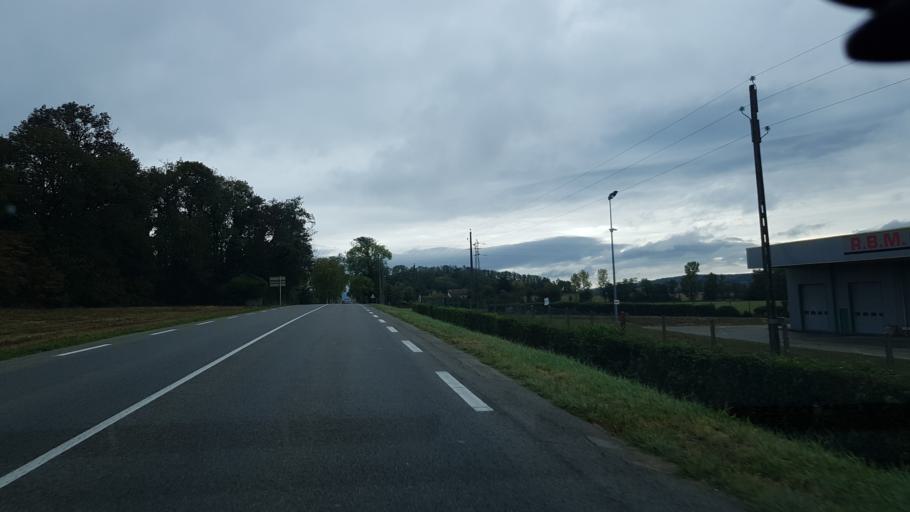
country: FR
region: Rhone-Alpes
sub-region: Departement de l'Ain
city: Saint-Martin-du-Mont
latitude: 46.0907
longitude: 5.3145
